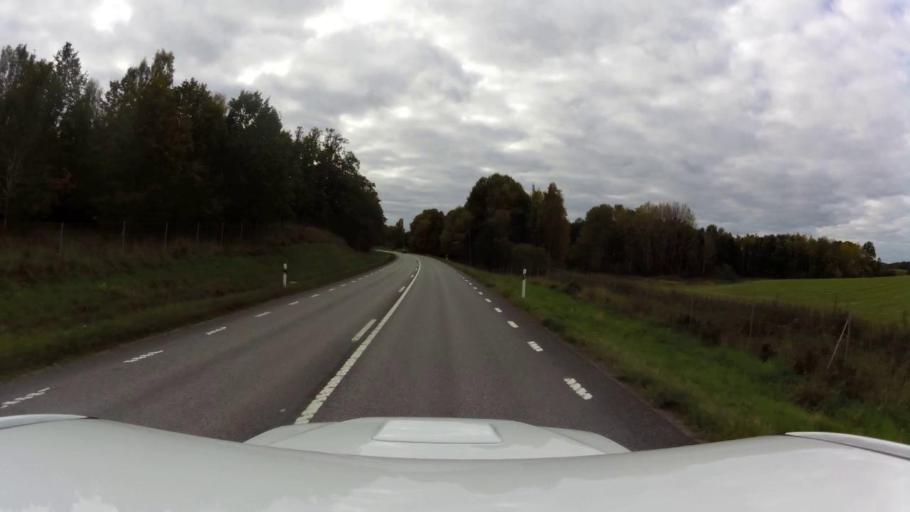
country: SE
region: OEstergoetland
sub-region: Kinda Kommun
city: Rimforsa
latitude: 58.1888
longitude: 15.6665
